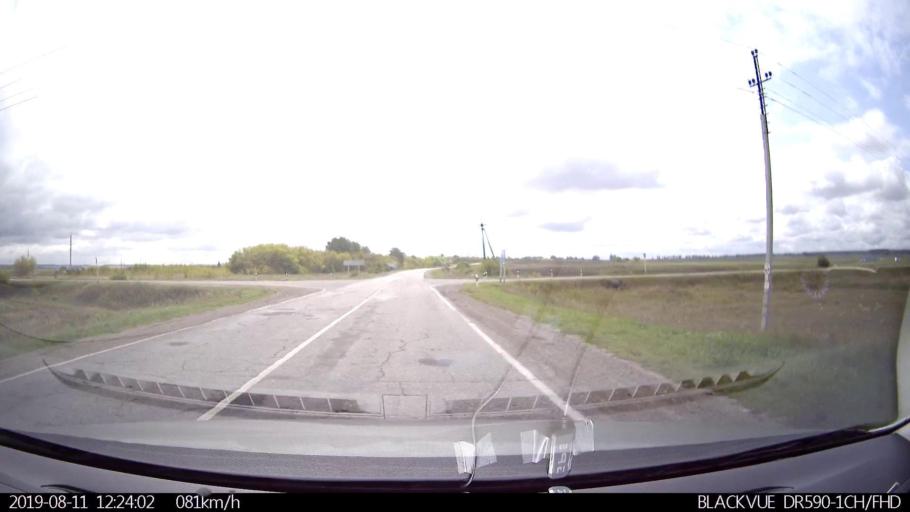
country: RU
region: Ulyanovsk
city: Ignatovka
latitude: 53.8880
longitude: 47.9501
